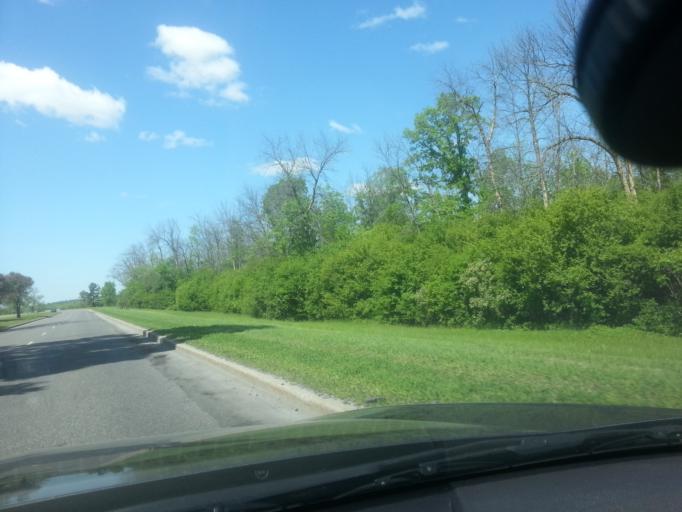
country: CA
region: Ontario
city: Ottawa
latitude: 45.4007
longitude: -75.7567
